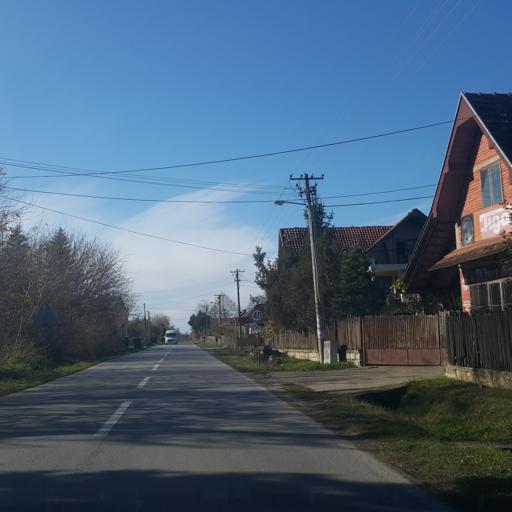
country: RS
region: Central Serbia
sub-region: Sumadijski Okrug
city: Topola
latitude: 44.2521
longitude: 20.7976
